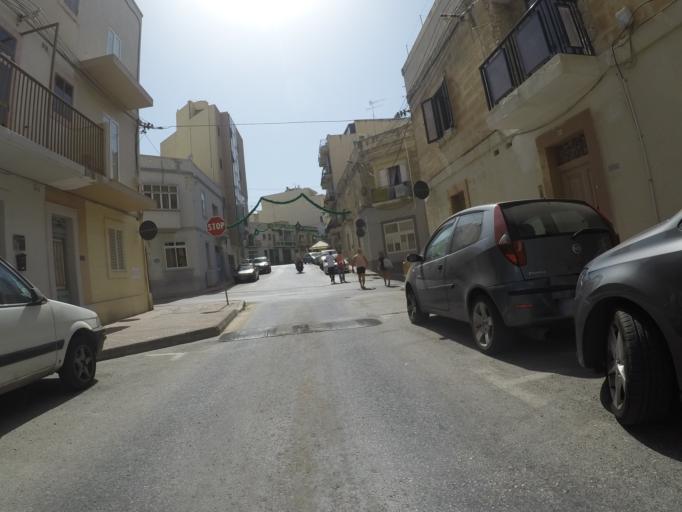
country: MT
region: Saint Paul's Bay
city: San Pawl il-Bahar
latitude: 35.9479
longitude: 14.4071
